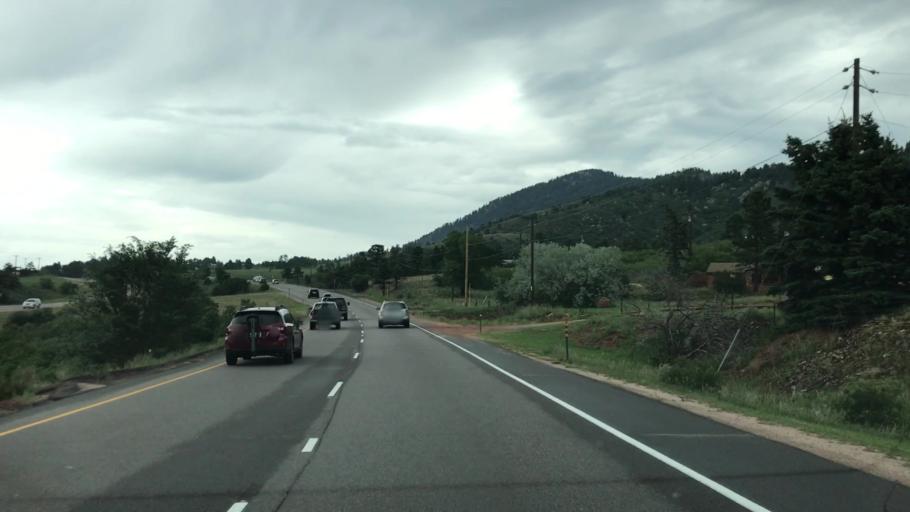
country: US
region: Colorado
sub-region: El Paso County
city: Cascade-Chipita Park
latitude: 38.9285
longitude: -104.9983
